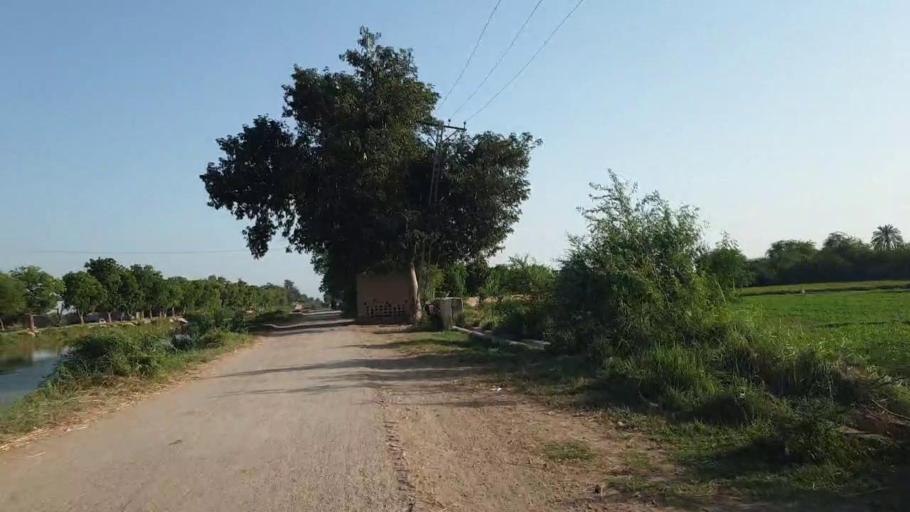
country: PK
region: Sindh
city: Hyderabad
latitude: 25.3206
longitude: 68.4277
